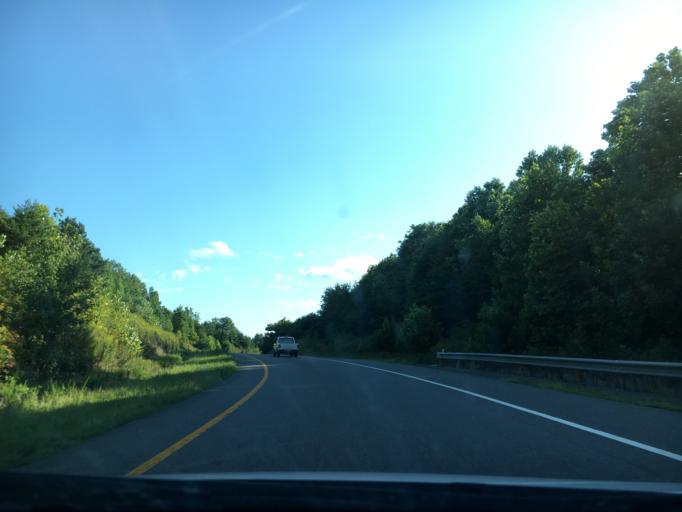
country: US
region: Virginia
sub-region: Amherst County
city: Madison Heights
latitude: 37.3885
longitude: -79.0939
